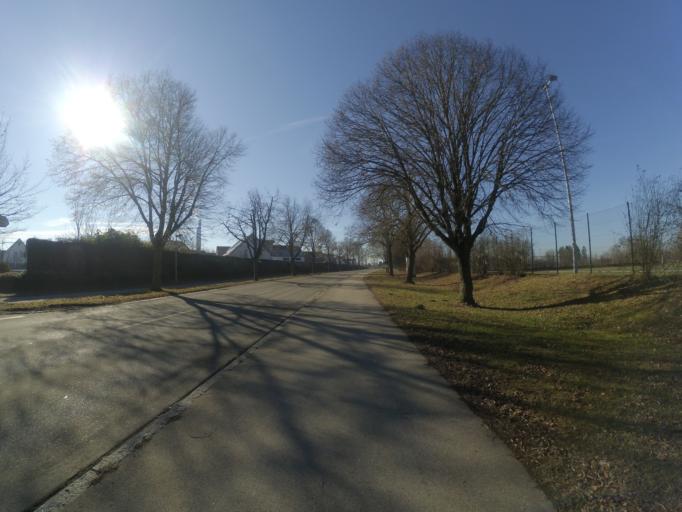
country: DE
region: Baden-Wuerttemberg
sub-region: Tuebingen Region
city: Erbach
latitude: 48.3337
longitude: 9.9346
